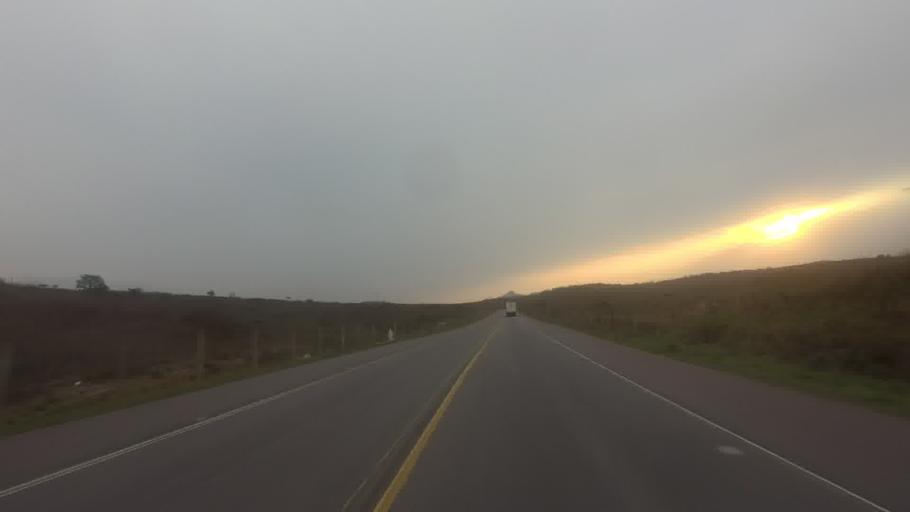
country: BR
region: Minas Gerais
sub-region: Recreio
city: Recreio
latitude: -21.6782
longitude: -42.3938
